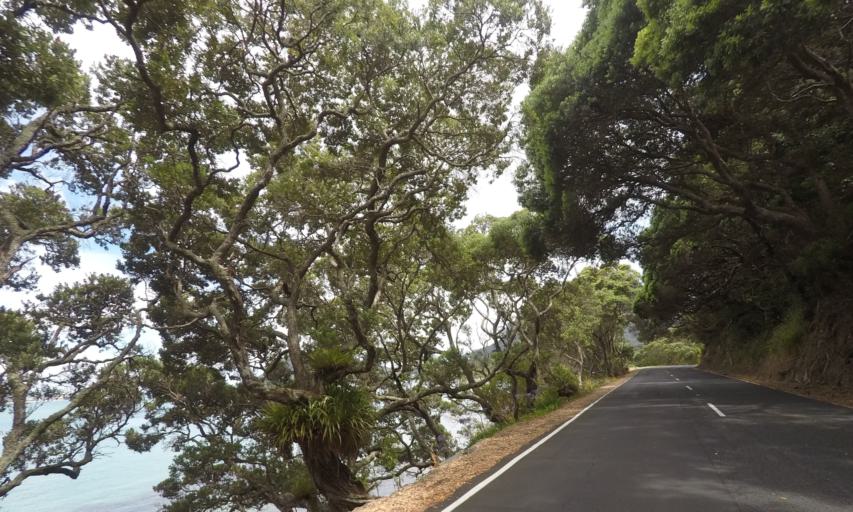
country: NZ
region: Northland
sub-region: Whangarei
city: Ruakaka
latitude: -35.8378
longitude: 174.5337
